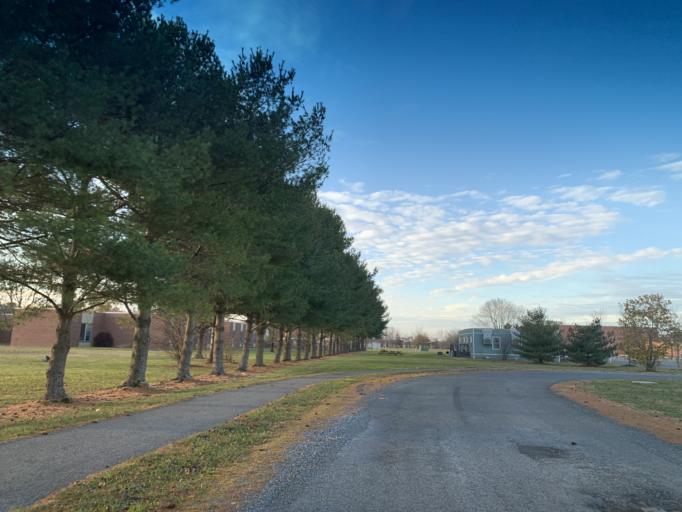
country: US
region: Maryland
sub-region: Kent County
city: Chestertown
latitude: 39.2831
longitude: -76.0920
